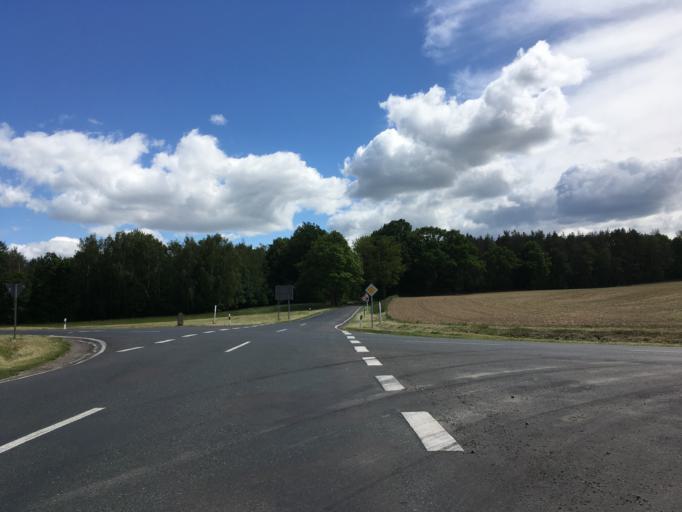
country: DE
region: Brandenburg
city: Protzel
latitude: 52.7062
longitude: 14.0146
